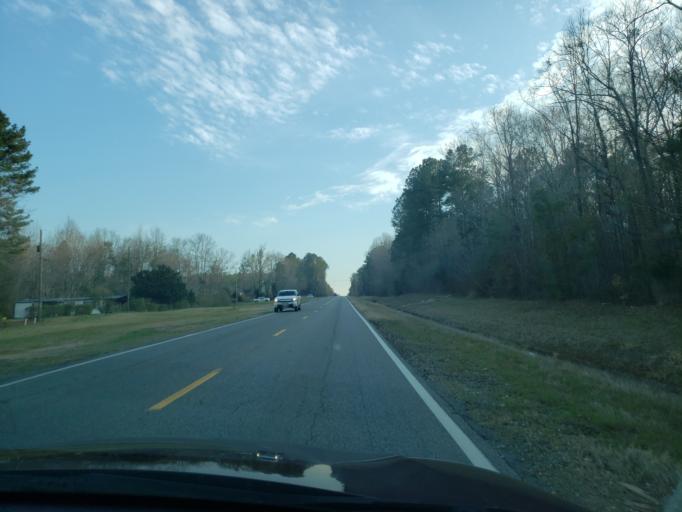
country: US
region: Alabama
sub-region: Hale County
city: Greensboro
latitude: 32.7593
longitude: -87.5853
